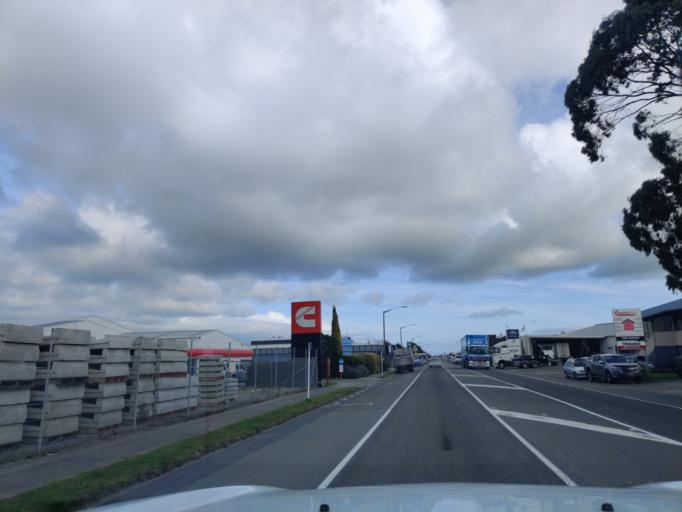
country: NZ
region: Manawatu-Wanganui
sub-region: Palmerston North City
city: Palmerston North
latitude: -40.3335
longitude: 175.6236
